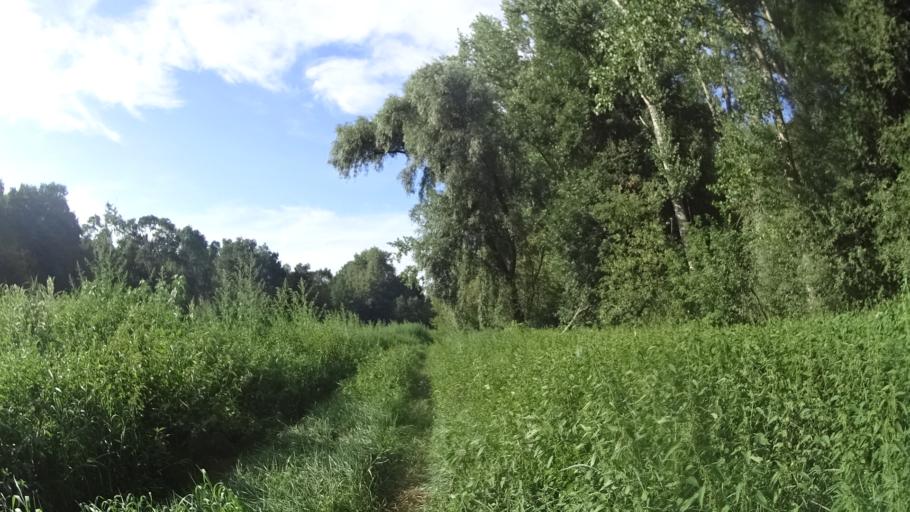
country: AT
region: Lower Austria
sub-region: Politischer Bezirk Mistelbach
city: Rabensburg
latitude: 48.6144
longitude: 16.9399
